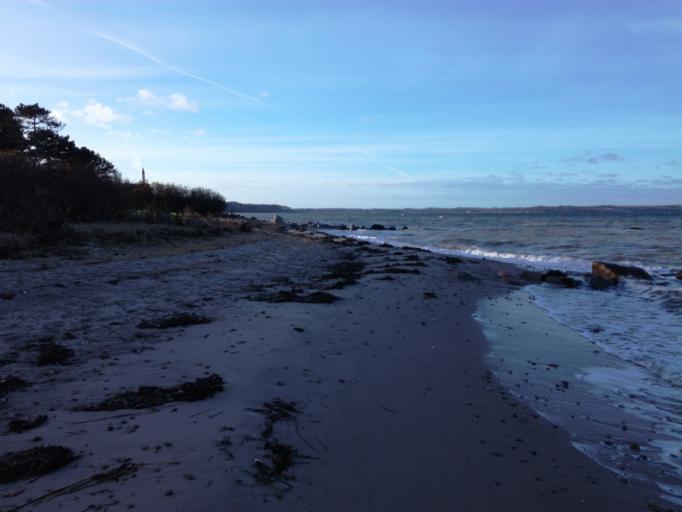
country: DK
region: South Denmark
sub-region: Fredericia Kommune
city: Fredericia
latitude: 55.6256
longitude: 9.7941
